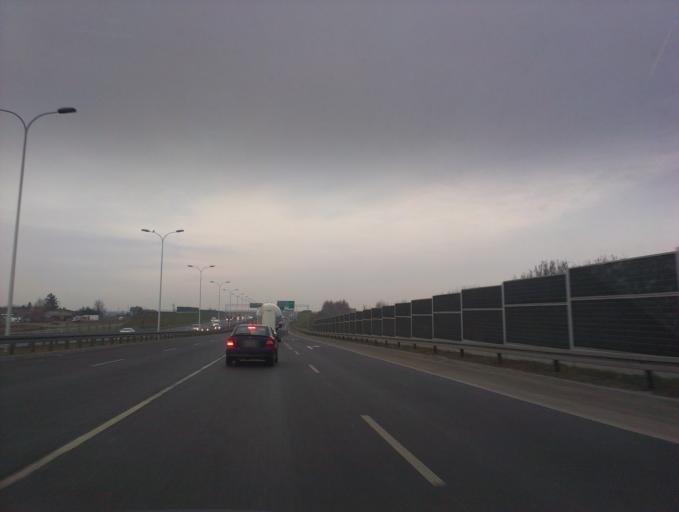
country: PL
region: Masovian Voivodeship
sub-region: Powiat pruszkowski
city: Nowe Grocholice
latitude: 52.1821
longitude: 20.9154
